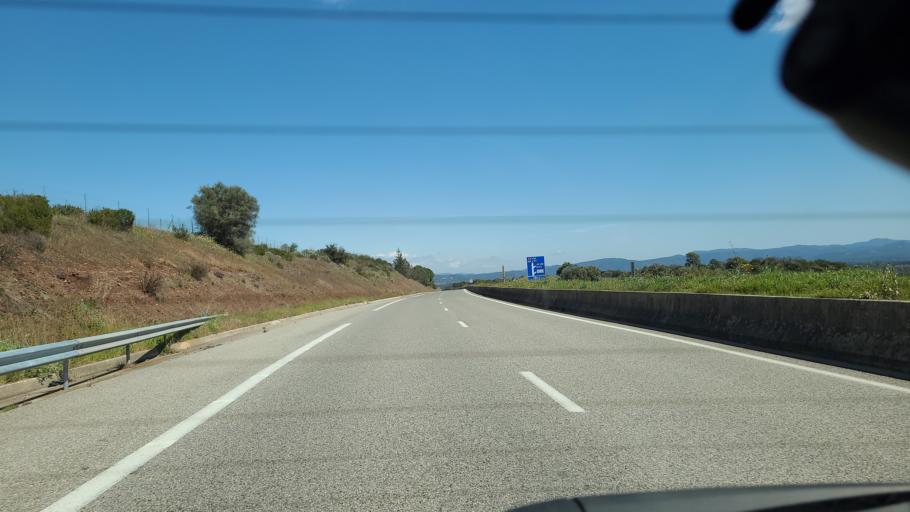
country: FR
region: Provence-Alpes-Cote d'Azur
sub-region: Departement du Var
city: Le Cannet-des-Maures
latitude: 43.3773
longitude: 6.3511
